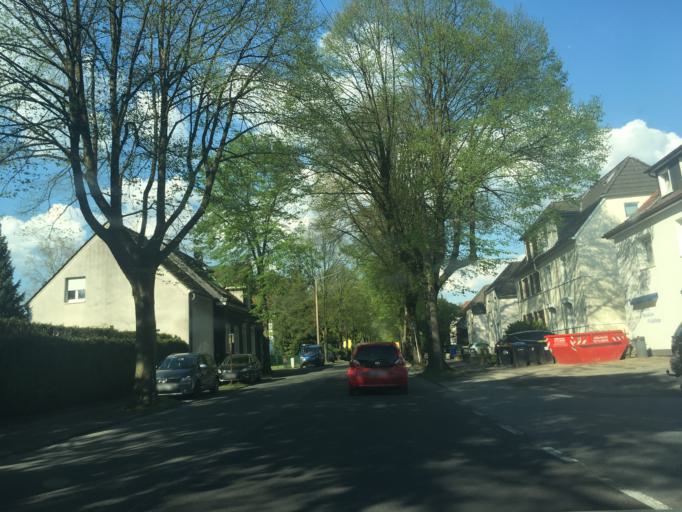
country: DE
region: North Rhine-Westphalia
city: Haan
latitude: 51.1836
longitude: 6.9885
